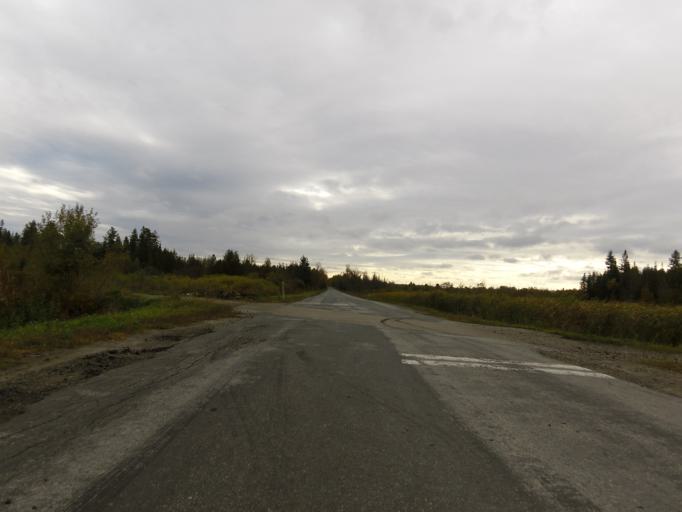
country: CA
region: Ontario
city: Arnprior
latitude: 45.4562
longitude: -76.1386
